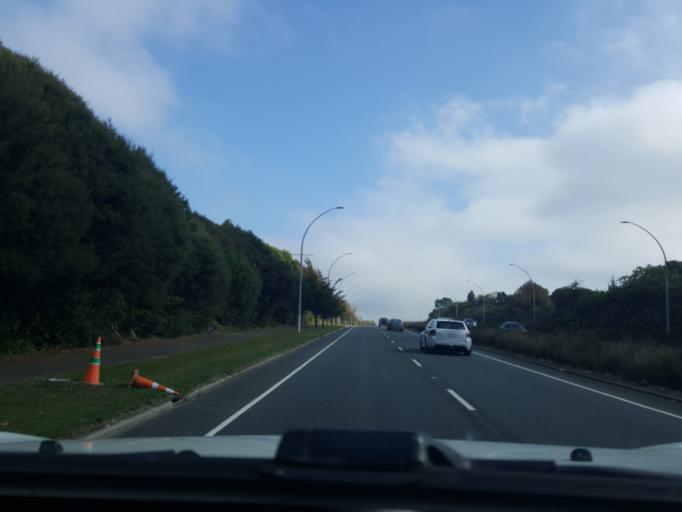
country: NZ
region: Waikato
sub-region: Hamilton City
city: Hamilton
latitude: -37.7458
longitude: 175.2475
